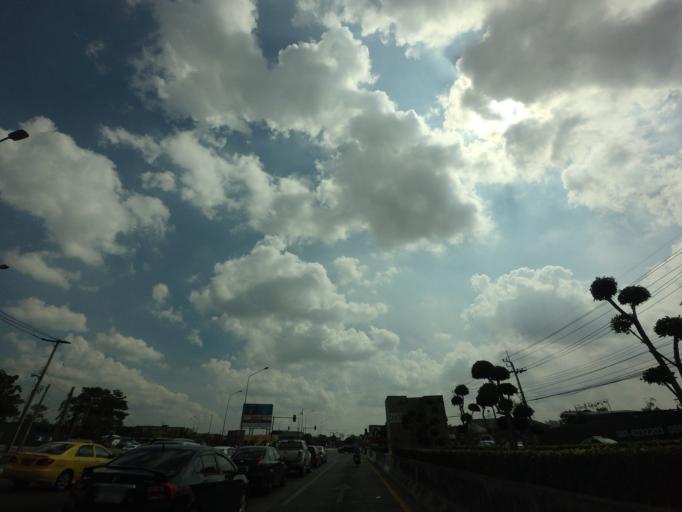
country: TH
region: Bangkok
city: Lat Phrao
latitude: 13.8160
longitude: 100.6416
